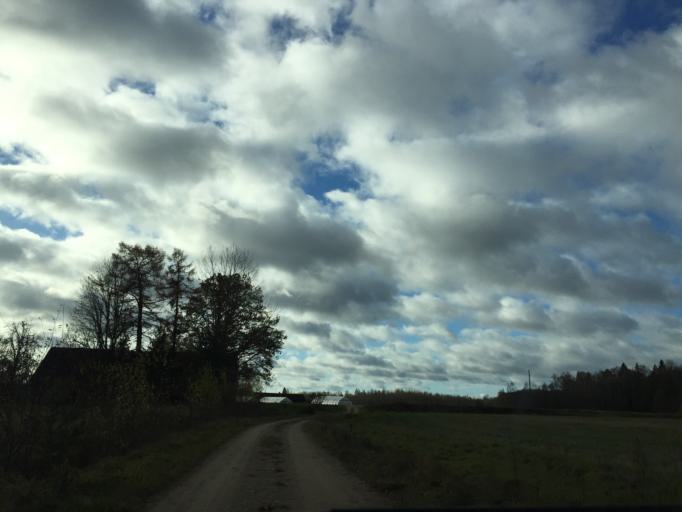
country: LV
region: Engure
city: Smarde
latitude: 56.9631
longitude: 23.2555
